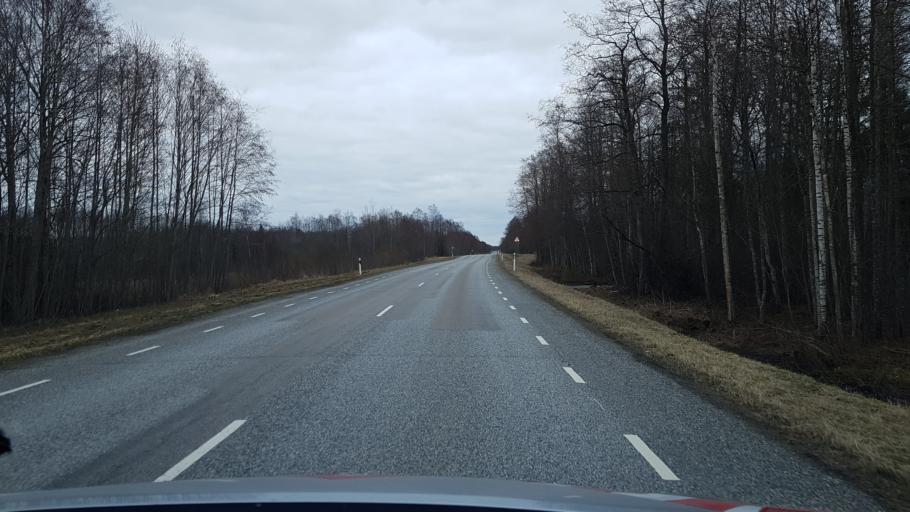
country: EE
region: Ida-Virumaa
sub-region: Narva-Joesuu linn
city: Narva-Joesuu
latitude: 59.3442
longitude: 27.9997
